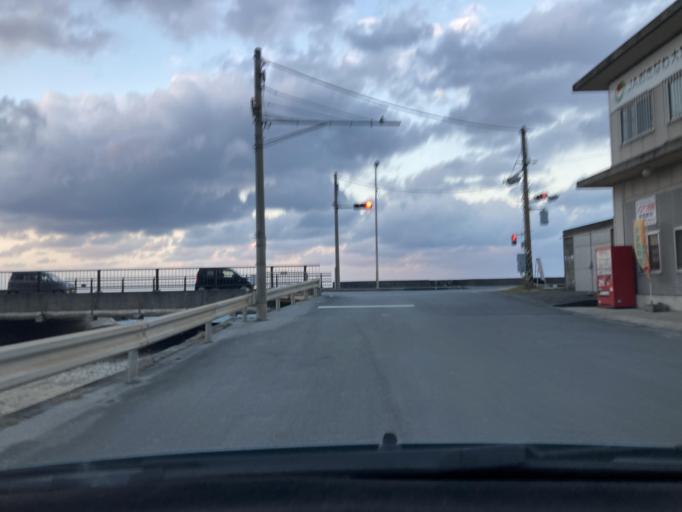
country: JP
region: Okinawa
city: Nago
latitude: 26.7029
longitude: 128.1201
